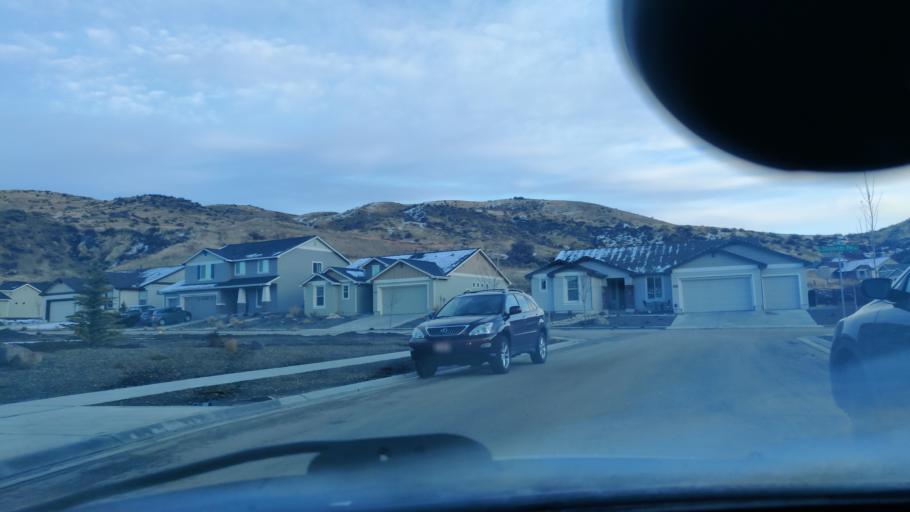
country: US
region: Idaho
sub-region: Ada County
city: Eagle
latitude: 43.7880
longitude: -116.2610
